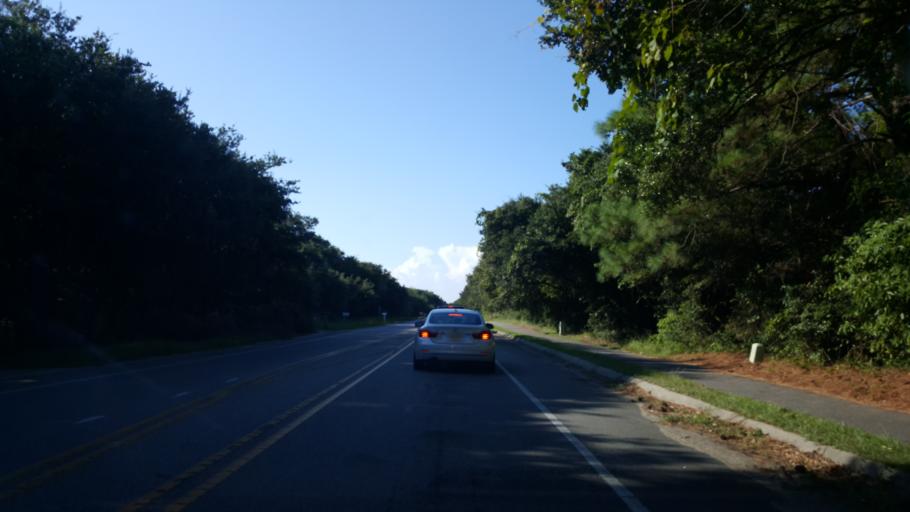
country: US
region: North Carolina
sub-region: Dare County
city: Southern Shores
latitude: 36.1354
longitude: -75.7353
